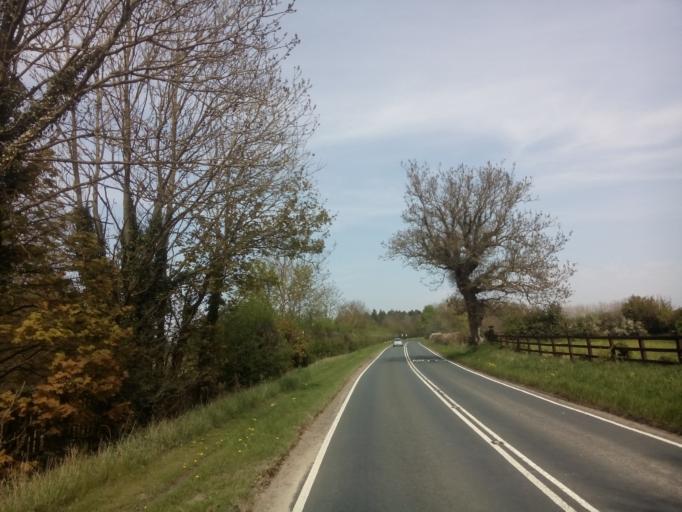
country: GB
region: England
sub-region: County Durham
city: West Rainton
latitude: 54.7930
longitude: -1.5128
